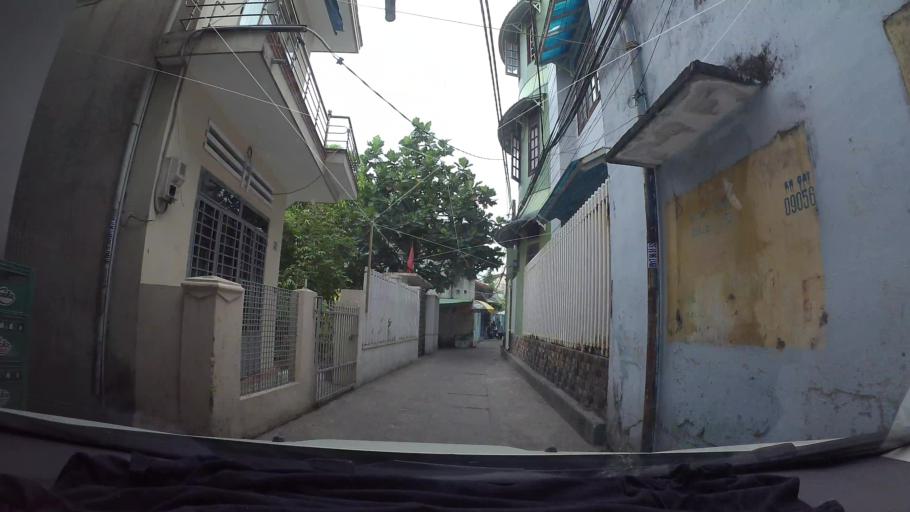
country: VN
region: Da Nang
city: Thanh Khe
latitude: 16.0714
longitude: 108.1898
